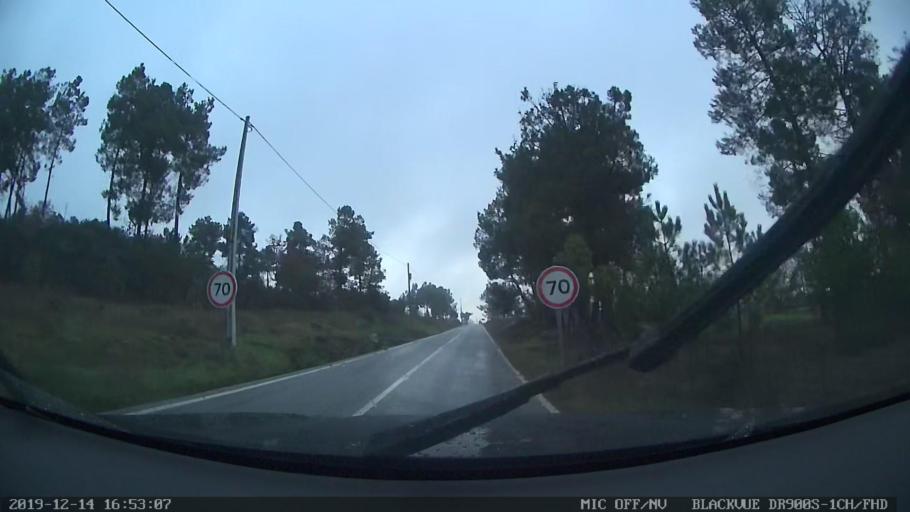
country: PT
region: Vila Real
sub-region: Murca
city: Murca
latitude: 41.4279
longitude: -7.5161
